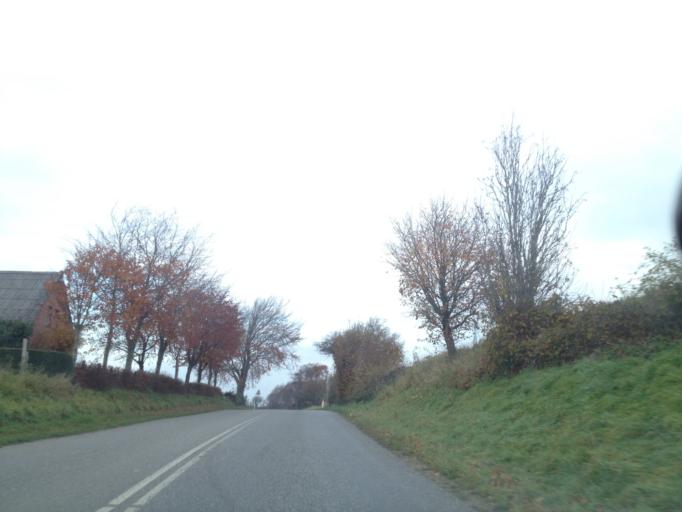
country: DK
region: South Denmark
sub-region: Assens Kommune
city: Vissenbjerg
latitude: 55.4054
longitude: 10.1570
